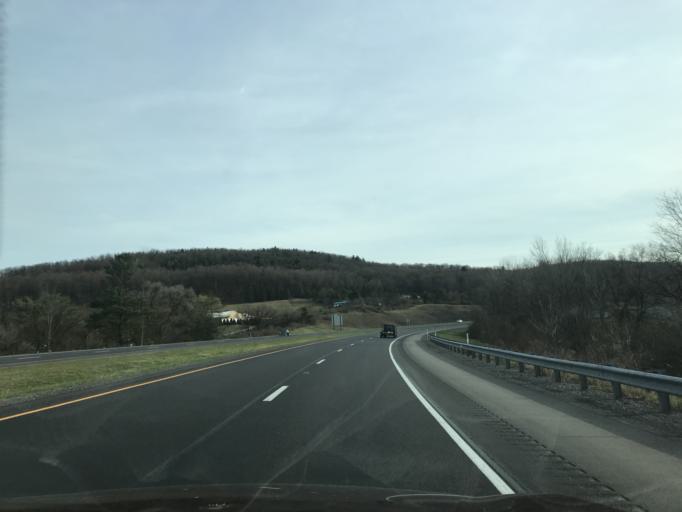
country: US
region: Pennsylvania
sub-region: Lycoming County
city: Muncy
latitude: 41.1941
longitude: -76.7698
